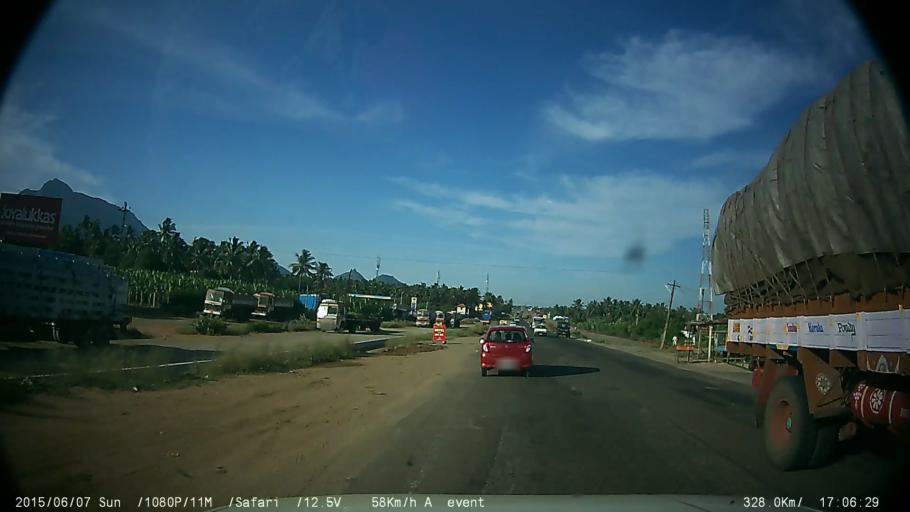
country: IN
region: Tamil Nadu
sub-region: Coimbatore
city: Madukkarai
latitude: 10.8627
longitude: 76.8722
